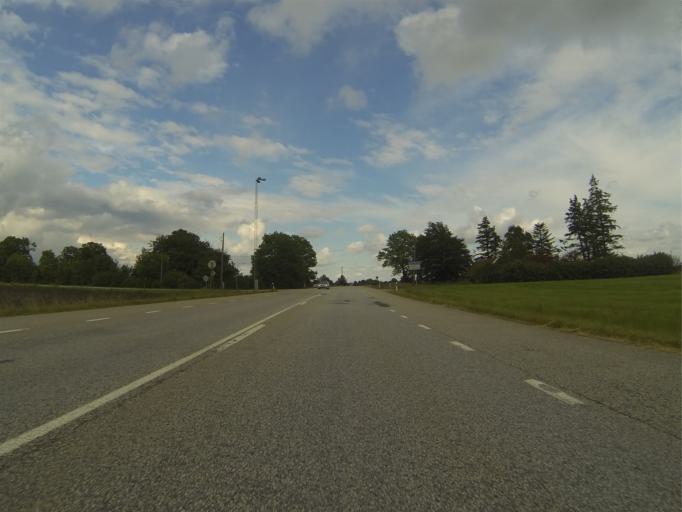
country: SE
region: Skane
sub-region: Staffanstorps Kommun
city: Hjaerup
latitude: 55.6426
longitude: 13.1353
